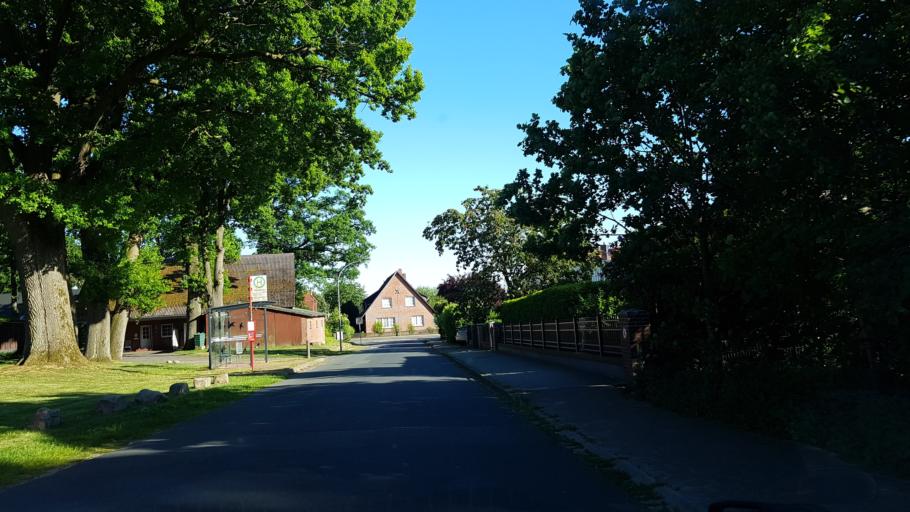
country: DE
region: Lower Saxony
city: Brackel
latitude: 53.3113
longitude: 10.0774
